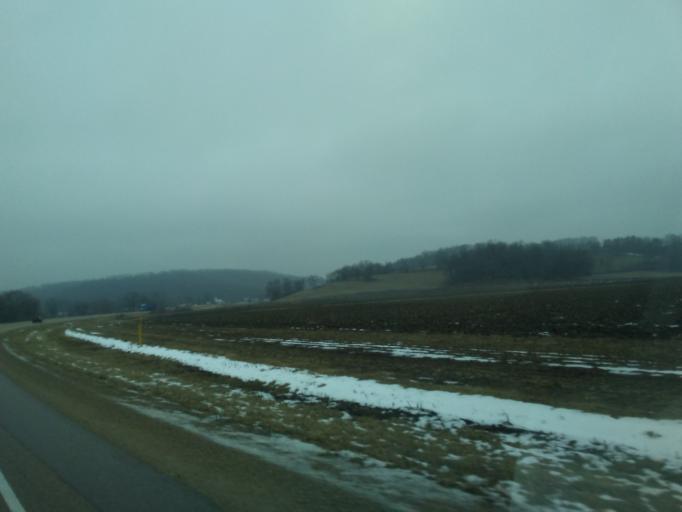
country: US
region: Wisconsin
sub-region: Dane County
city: Black Earth
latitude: 43.1367
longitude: -89.7377
